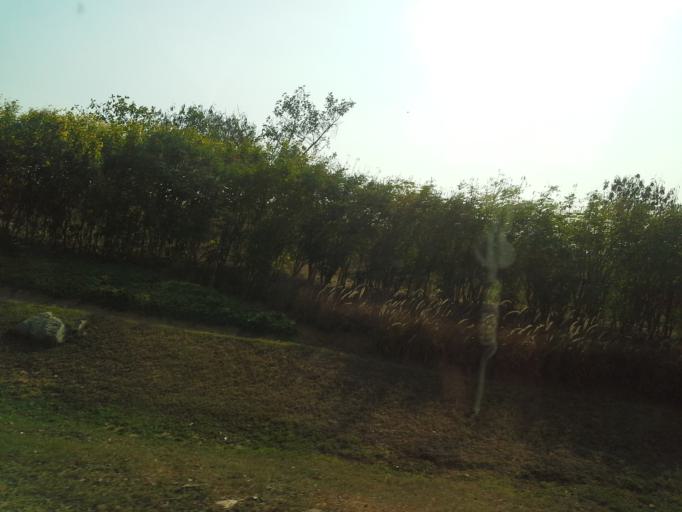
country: IN
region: Telangana
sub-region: Rangareddi
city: Balapur
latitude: 17.2431
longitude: 78.4079
